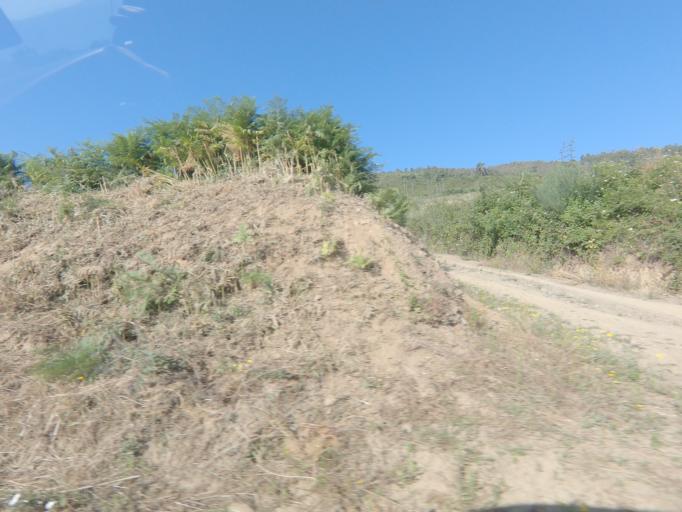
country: PT
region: Vila Real
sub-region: Sabrosa
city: Vilela
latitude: 41.2323
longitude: -7.5705
